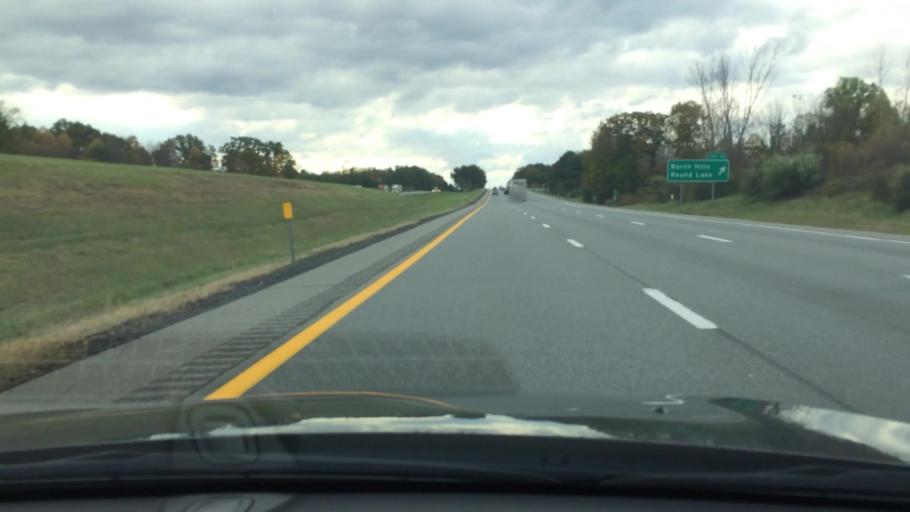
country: US
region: New York
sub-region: Saratoga County
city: Country Knolls
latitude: 42.9428
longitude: -73.8056
